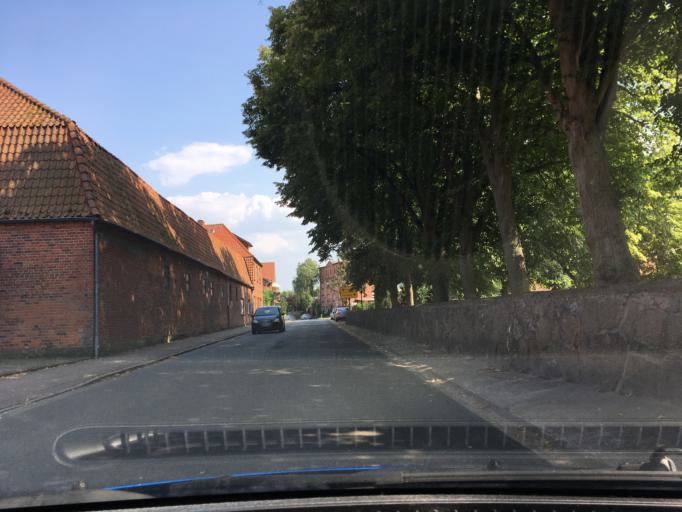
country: DE
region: Lower Saxony
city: Tosterglope
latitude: 53.2435
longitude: 10.7852
